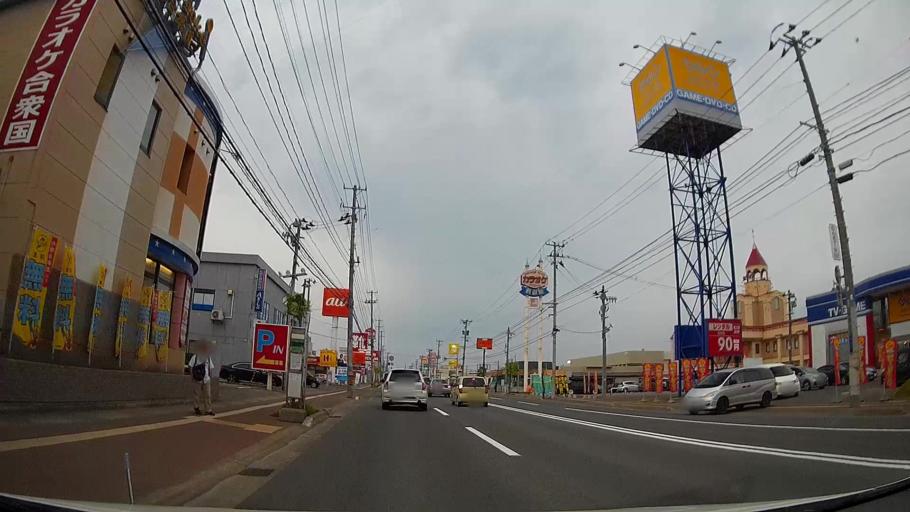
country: JP
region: Aomori
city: Aomori Shi
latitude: 40.8013
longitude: 140.7568
